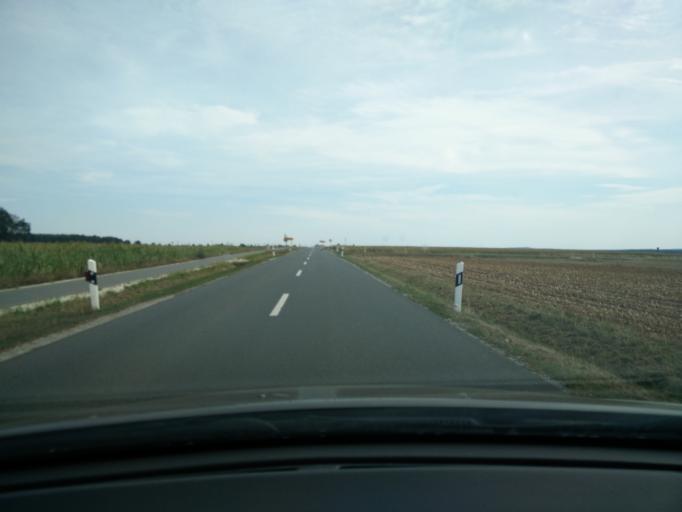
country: DE
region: Bavaria
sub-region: Regierungsbezirk Mittelfranken
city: Puschendorf
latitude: 49.5334
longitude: 10.8009
